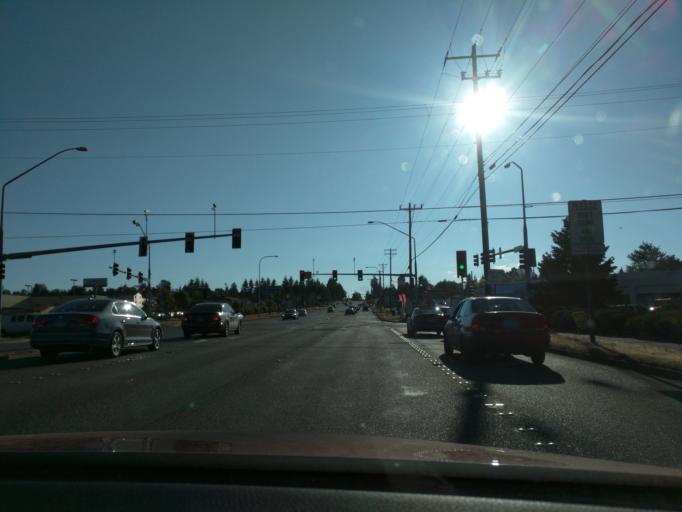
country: US
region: Washington
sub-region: Snohomish County
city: Martha Lake
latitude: 47.8820
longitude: -122.2381
